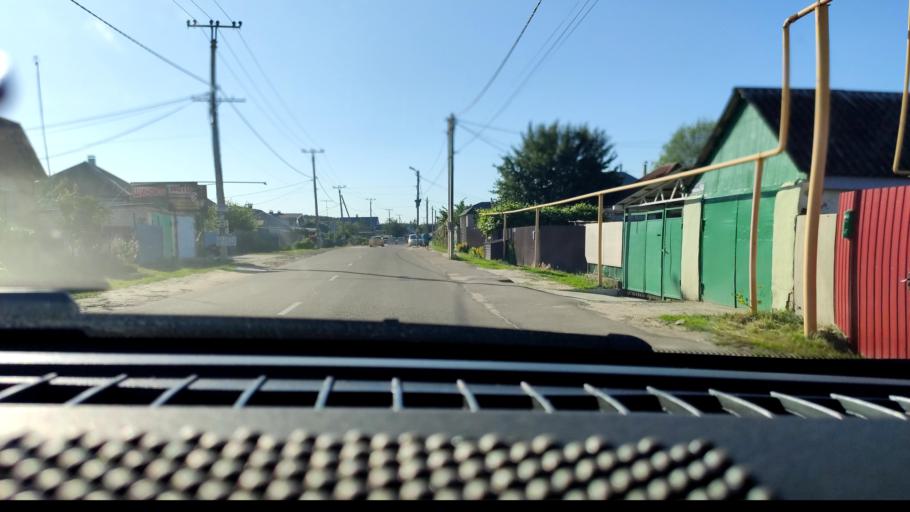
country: RU
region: Voronezj
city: Somovo
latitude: 51.7554
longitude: 39.4329
